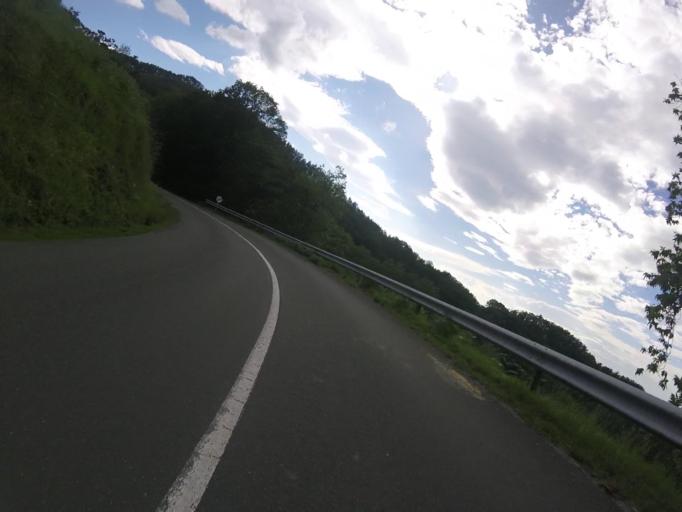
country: ES
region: Navarre
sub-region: Provincia de Navarra
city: Arano
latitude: 43.2527
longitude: -1.8468
